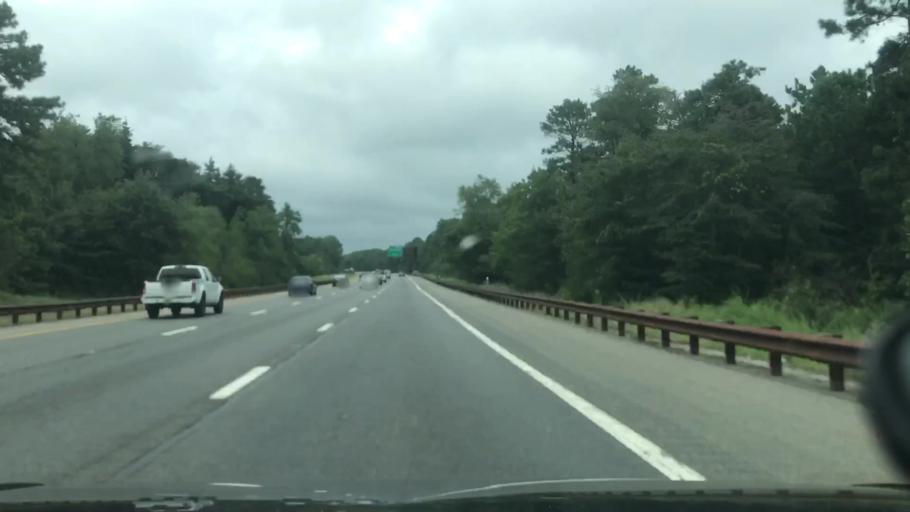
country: US
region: New Jersey
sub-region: Ocean County
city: Forked River
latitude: 39.8293
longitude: -74.2257
